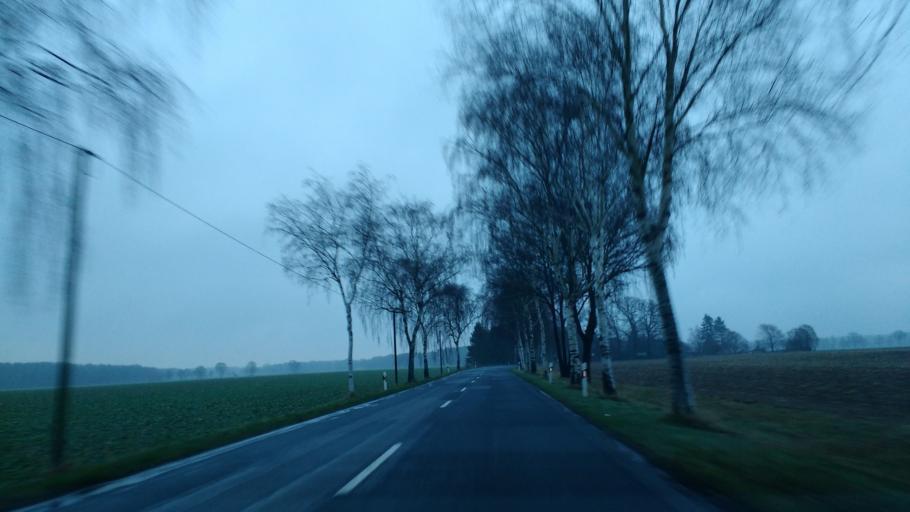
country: DE
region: Lower Saxony
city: Gilten
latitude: 52.6400
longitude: 9.5081
